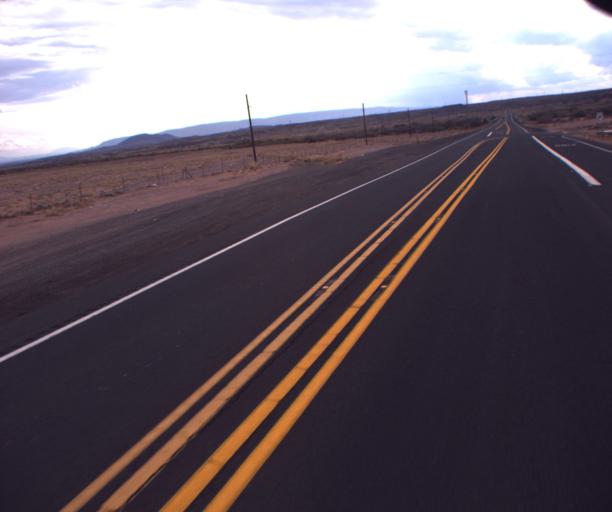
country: US
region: Arizona
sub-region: Coconino County
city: Tuba City
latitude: 36.0801
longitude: -111.3755
